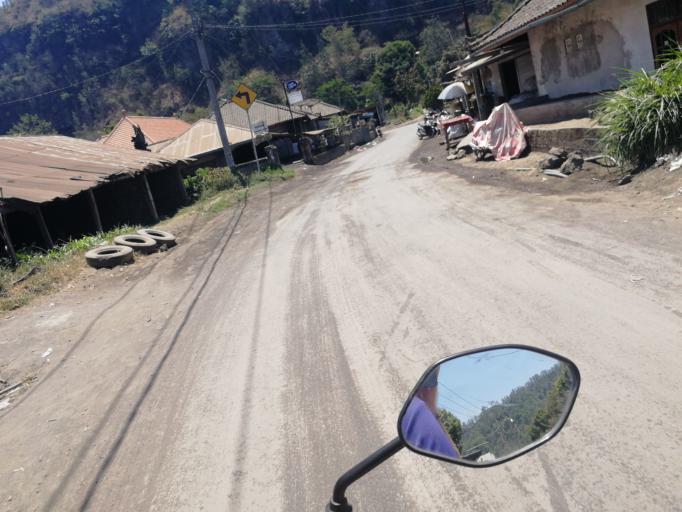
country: ID
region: Bali
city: Banjar Trunyan
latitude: -8.2238
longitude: 115.4102
